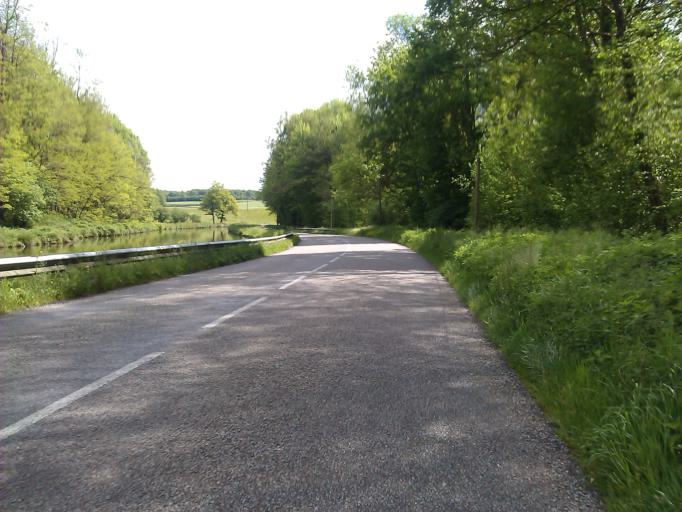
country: FR
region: Bourgogne
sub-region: Departement de Saone-et-Loire
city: Ecuisses
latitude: 46.7900
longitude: 4.5572
